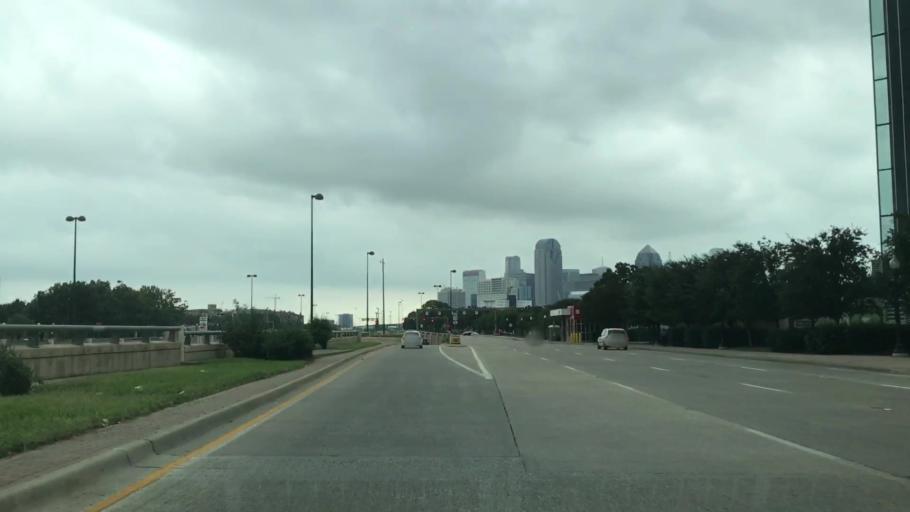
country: US
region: Texas
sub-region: Dallas County
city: Highland Park
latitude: 32.8067
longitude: -96.7937
